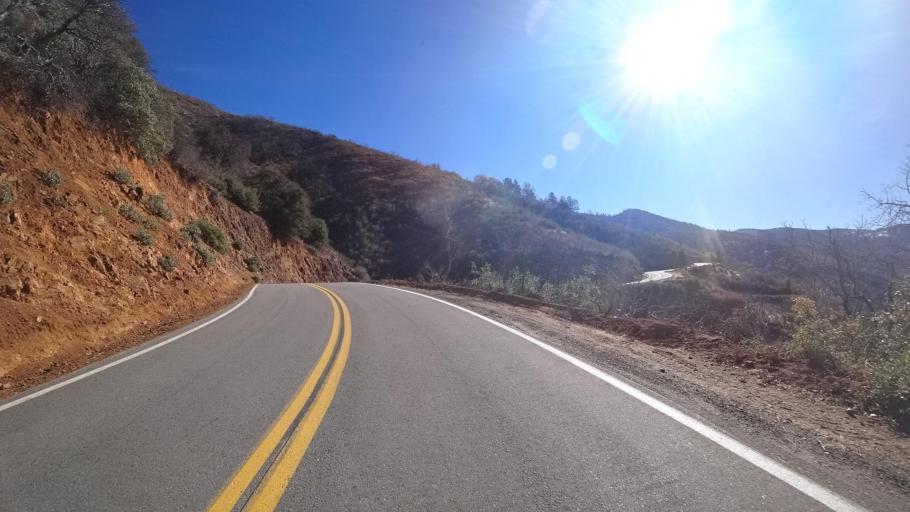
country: US
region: California
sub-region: Kern County
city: Alta Sierra
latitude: 35.7461
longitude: -118.5825
